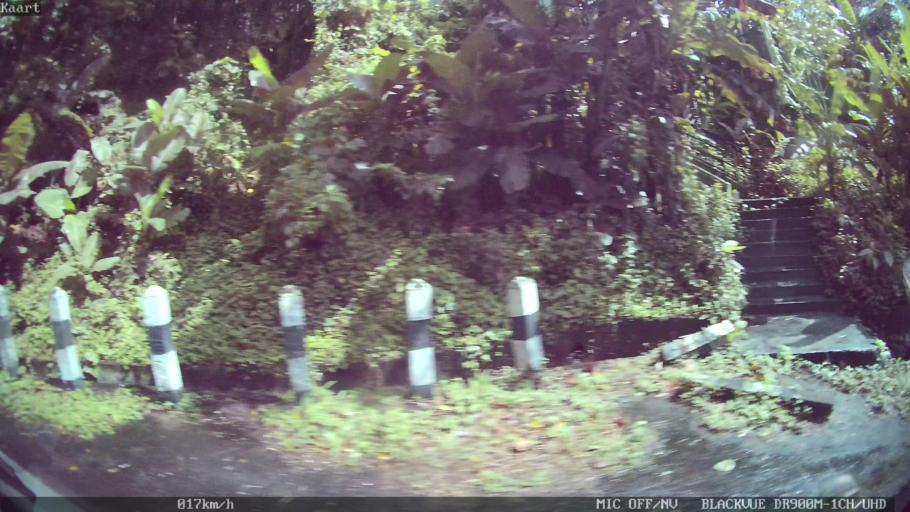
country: ID
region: Bali
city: Banjar Tebongkang
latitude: -8.5473
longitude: 115.2526
